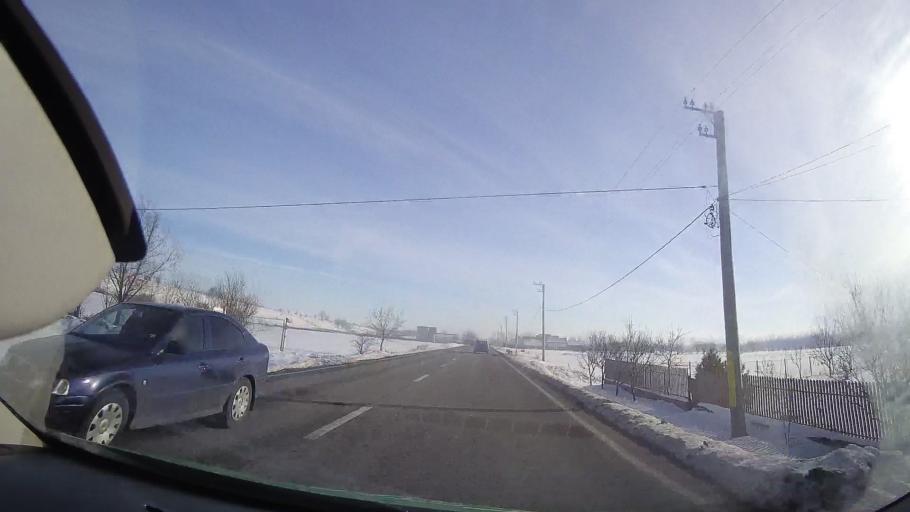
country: RO
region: Neamt
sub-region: Comuna Ghindaoani
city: Ghindaoani
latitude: 47.0853
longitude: 26.3355
